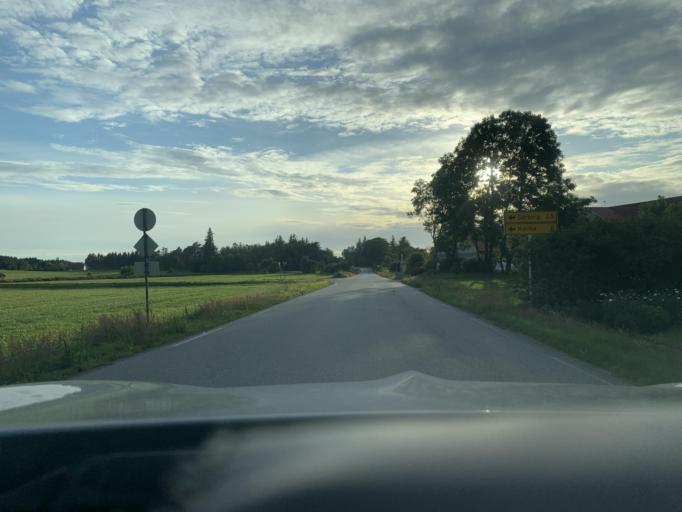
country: NO
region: Rogaland
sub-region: Ha
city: Naerbo
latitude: 58.6845
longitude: 5.7457
